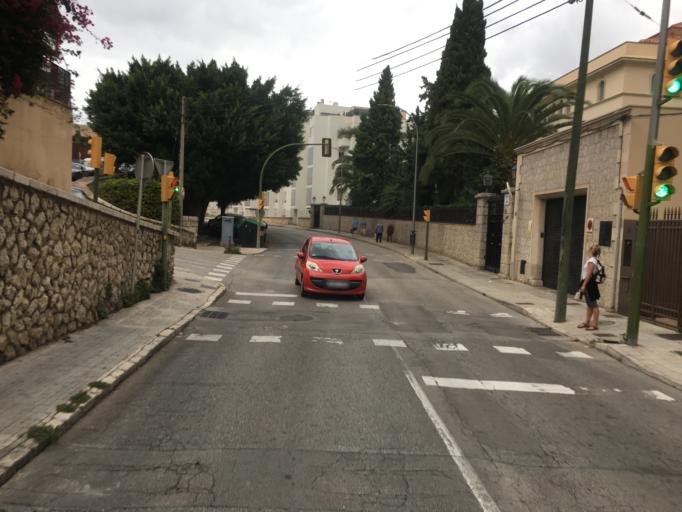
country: ES
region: Balearic Islands
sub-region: Illes Balears
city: Palma
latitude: 39.5552
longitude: 2.6235
